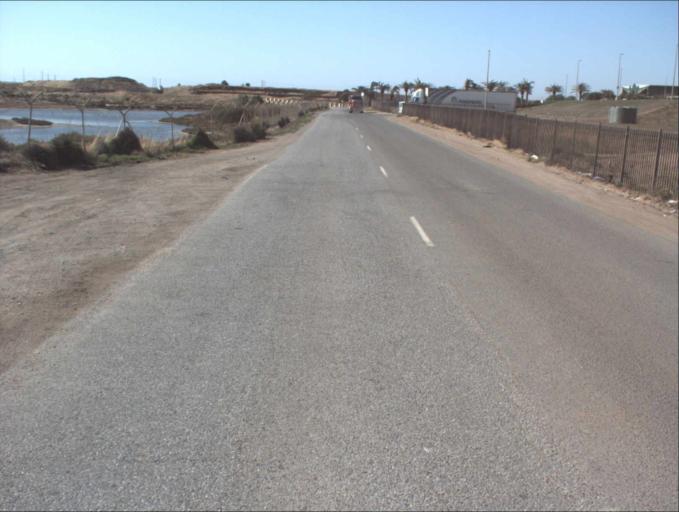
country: AU
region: South Australia
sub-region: Port Adelaide Enfield
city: Alberton
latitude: -34.8321
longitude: 138.5460
